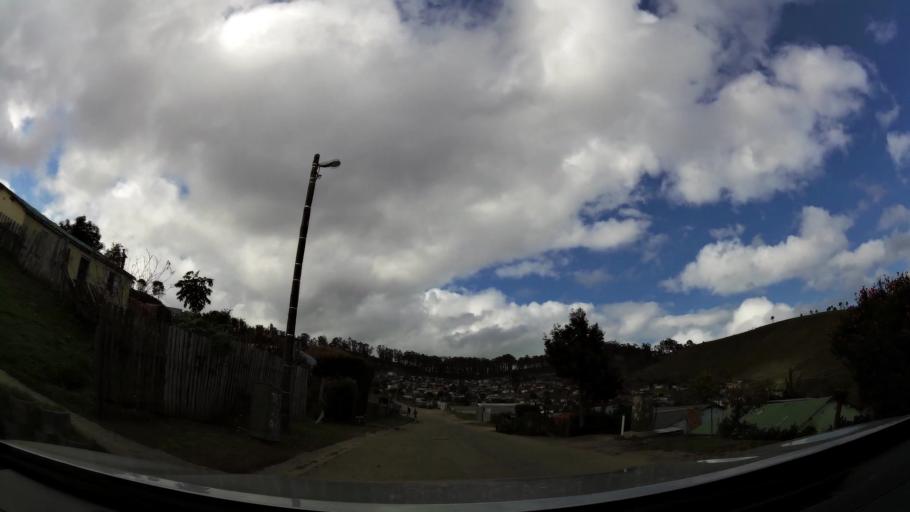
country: ZA
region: Western Cape
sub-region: Eden District Municipality
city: Knysna
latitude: -34.0520
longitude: 23.0991
